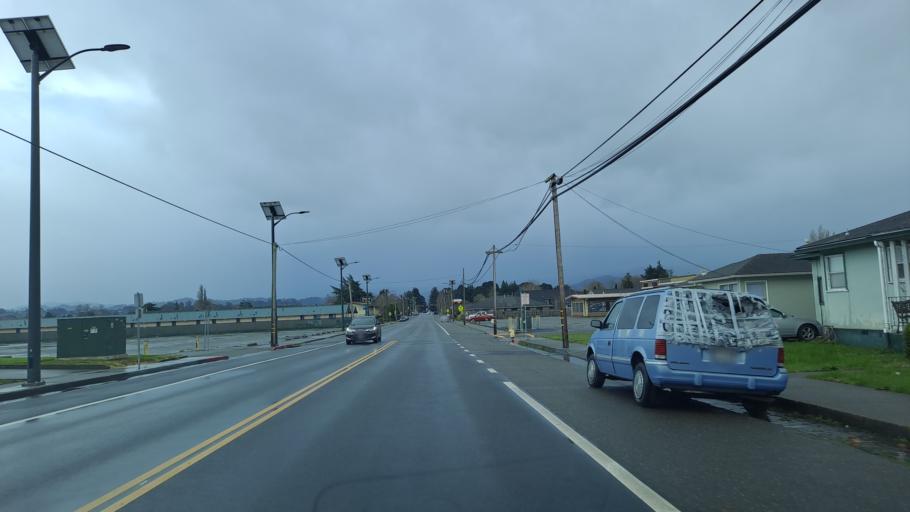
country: US
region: California
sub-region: Humboldt County
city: Fortuna
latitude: 40.5945
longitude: -124.1545
